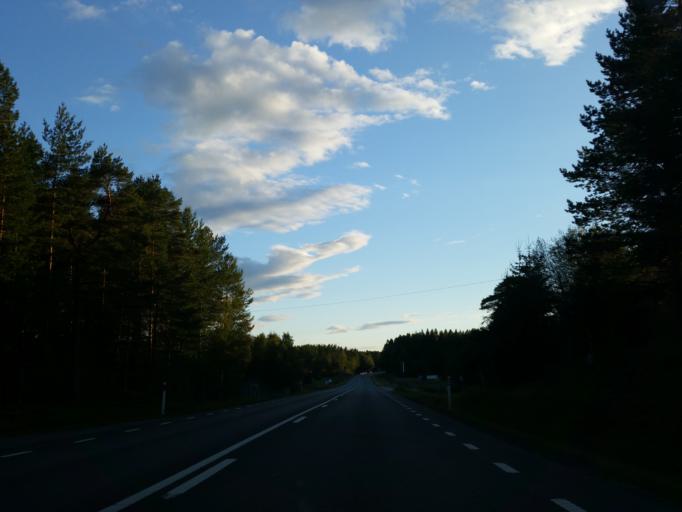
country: SE
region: Vaesterbotten
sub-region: Robertsfors Kommun
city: Robertsfors
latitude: 64.0047
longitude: 20.8006
